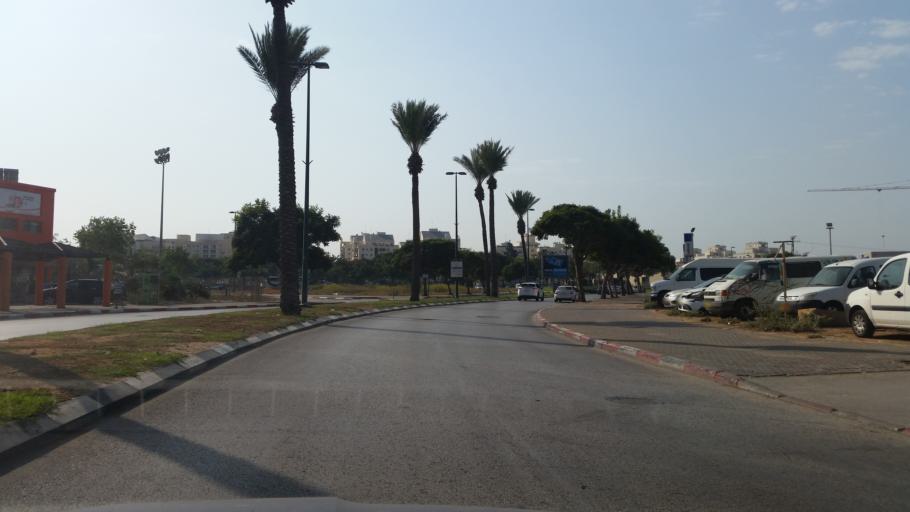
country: IL
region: Central District
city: Bet Yizhaq
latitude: 32.3138
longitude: 34.8734
